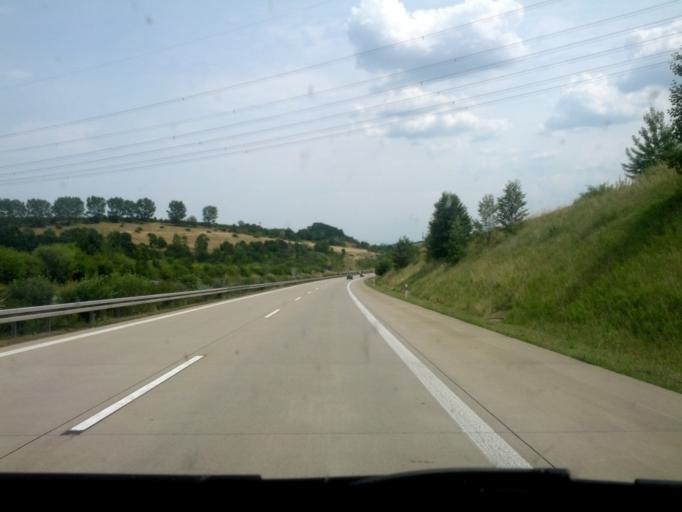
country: DE
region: Saxony
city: Dohna
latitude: 50.9688
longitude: 13.8357
